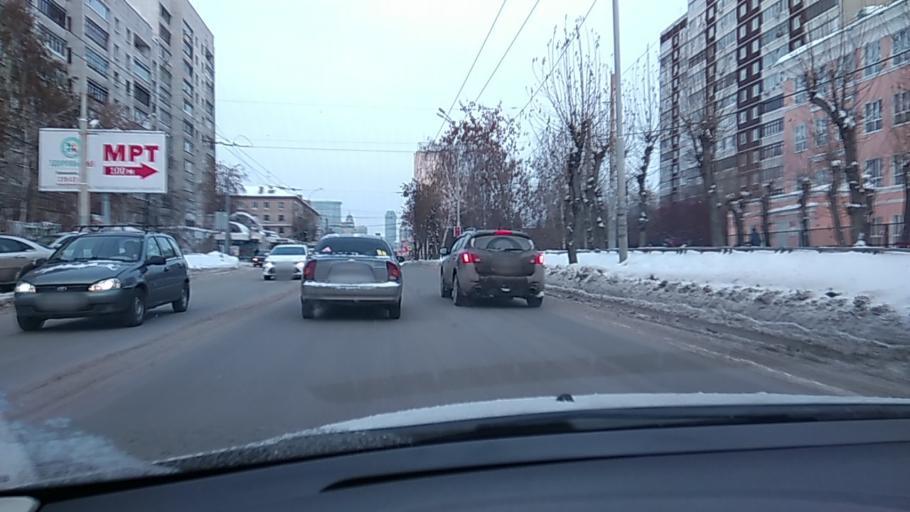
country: RU
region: Sverdlovsk
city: Yekaterinburg
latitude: 56.8130
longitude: 60.6219
